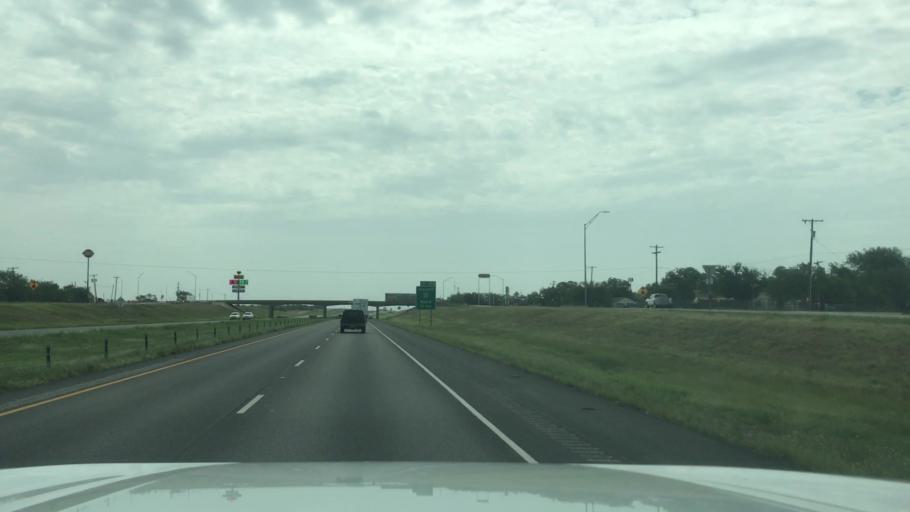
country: US
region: Texas
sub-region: Callahan County
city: Baird
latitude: 32.4027
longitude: -99.3895
